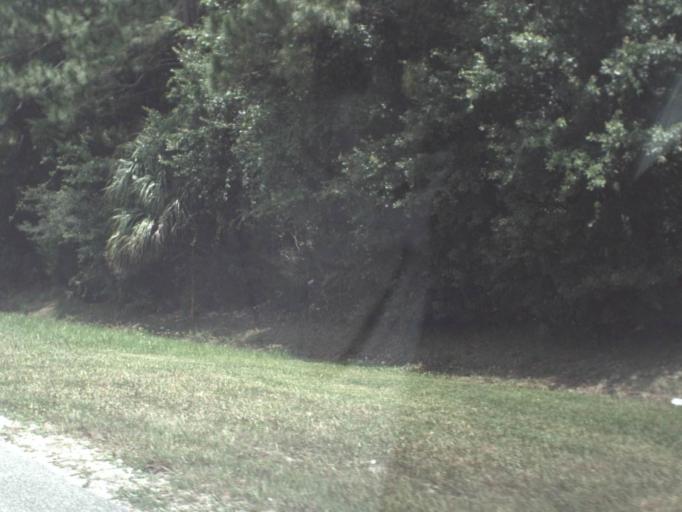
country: US
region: Florida
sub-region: Putnam County
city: Palatka
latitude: 29.6595
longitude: -81.6720
